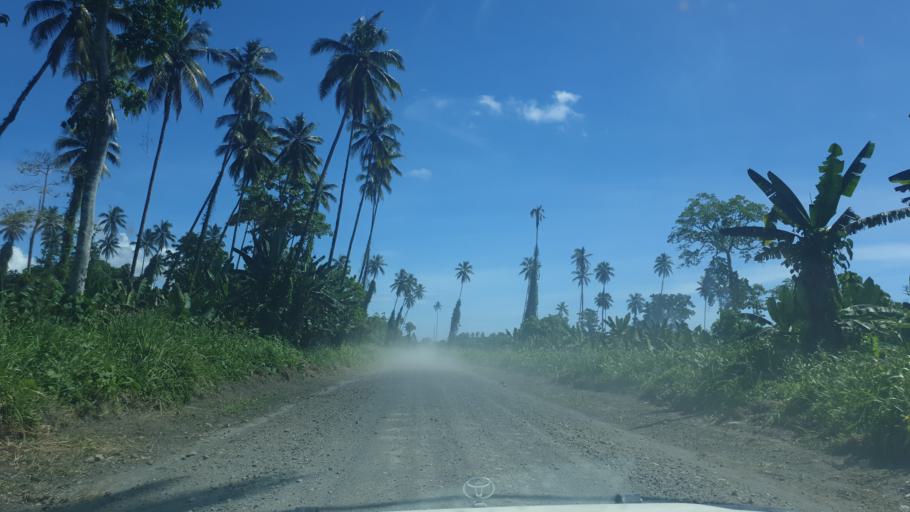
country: PG
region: Bougainville
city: Arawa
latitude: -5.9753
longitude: 155.3487
